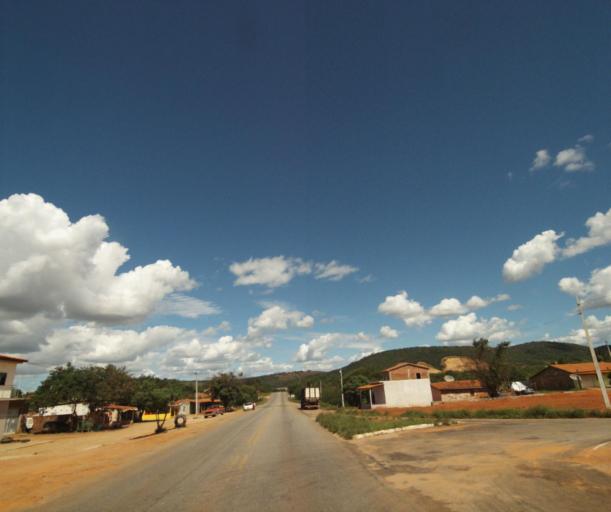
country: BR
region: Bahia
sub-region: Caetite
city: Caetite
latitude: -14.1698
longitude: -42.2297
